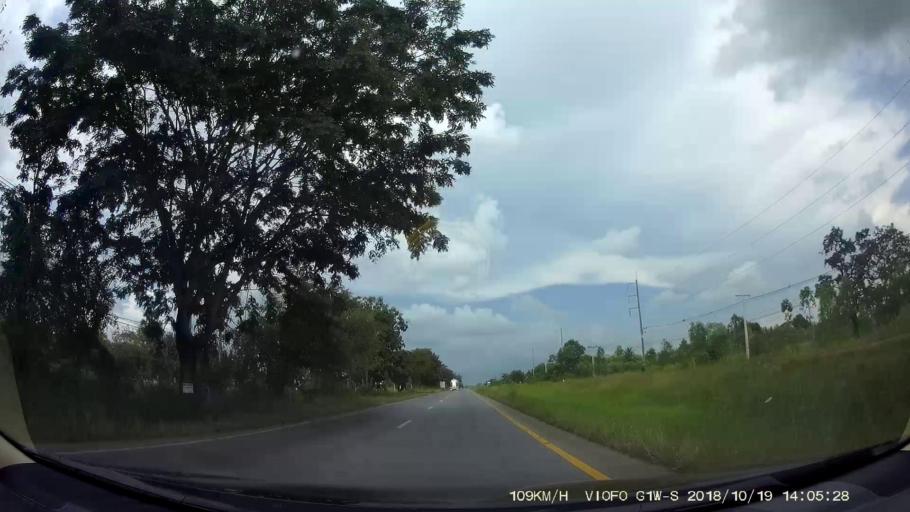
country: TH
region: Chaiyaphum
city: Chaiyaphum
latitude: 15.8757
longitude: 102.0935
